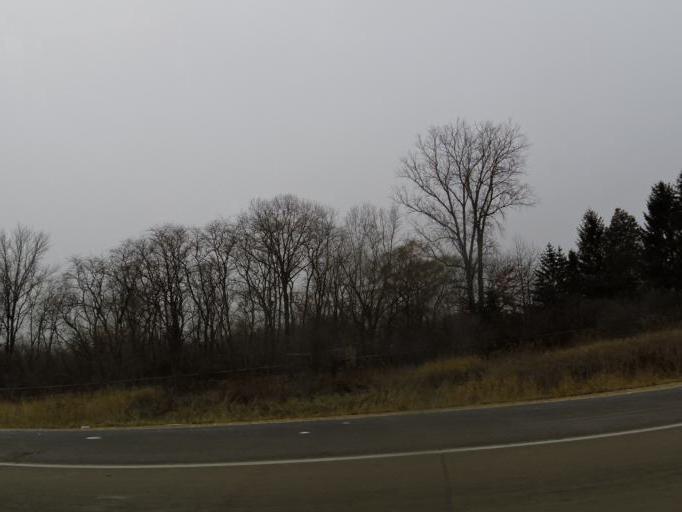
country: US
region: Minnesota
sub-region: Washington County
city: Oakdale
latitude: 44.9793
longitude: -92.9599
